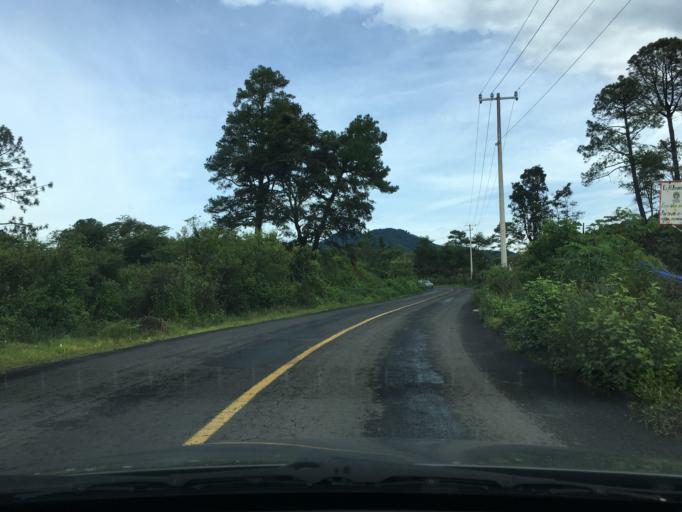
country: MX
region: Michoacan
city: Nuevo San Juan Parangaricutiro
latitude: 19.4275
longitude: -102.1387
